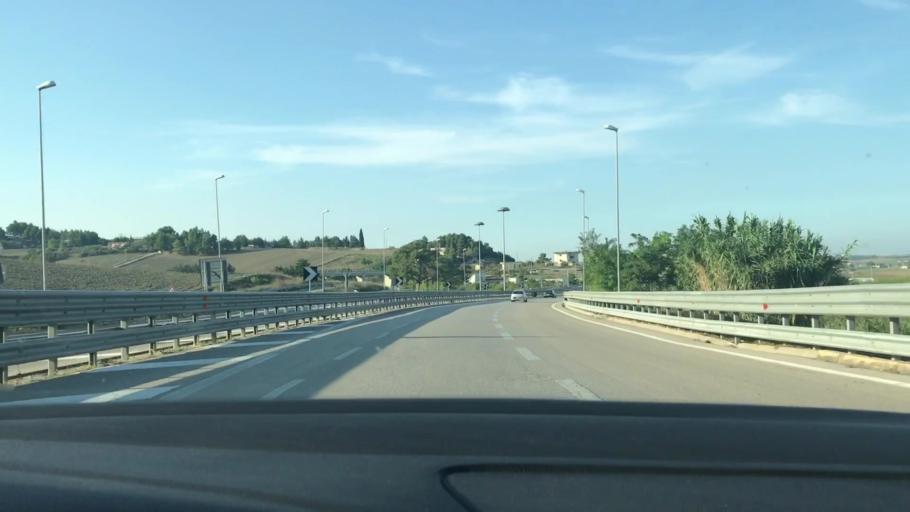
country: IT
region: Basilicate
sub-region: Provincia di Matera
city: Matera
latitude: 40.6882
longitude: 16.5901
